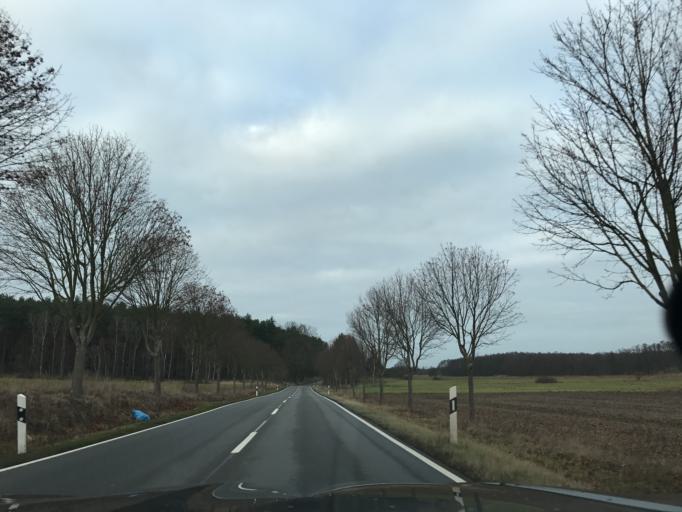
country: DE
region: Brandenburg
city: Brandenburg an der Havel
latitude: 52.3548
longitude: 12.6091
